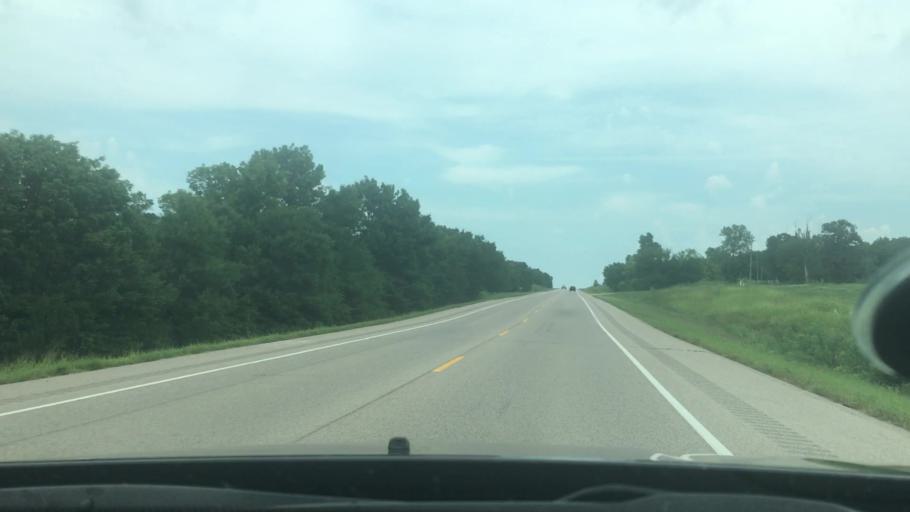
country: US
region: Oklahoma
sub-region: Seminole County
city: Konawa
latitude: 35.0082
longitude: -96.6788
